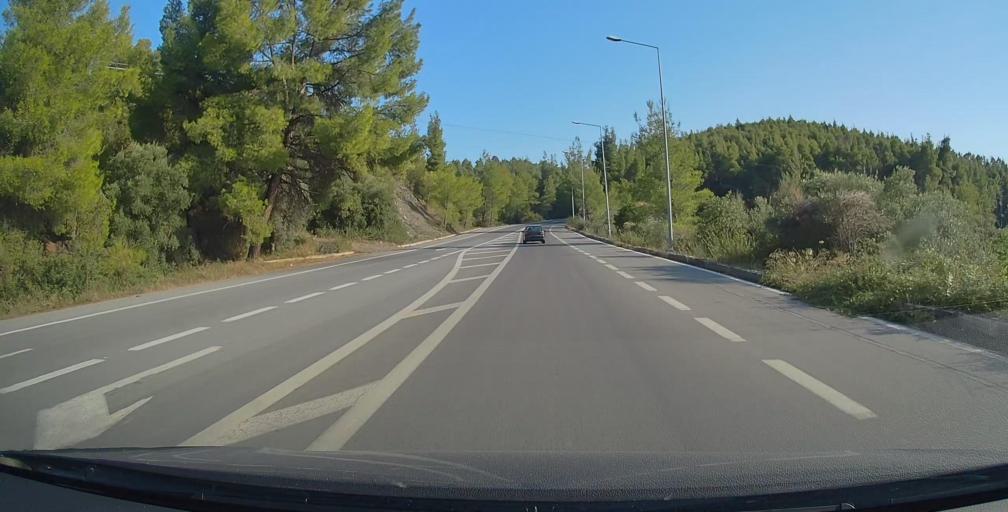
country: GR
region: Central Macedonia
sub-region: Nomos Chalkidikis
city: Neos Marmaras
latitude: 40.0779
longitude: 23.8052
